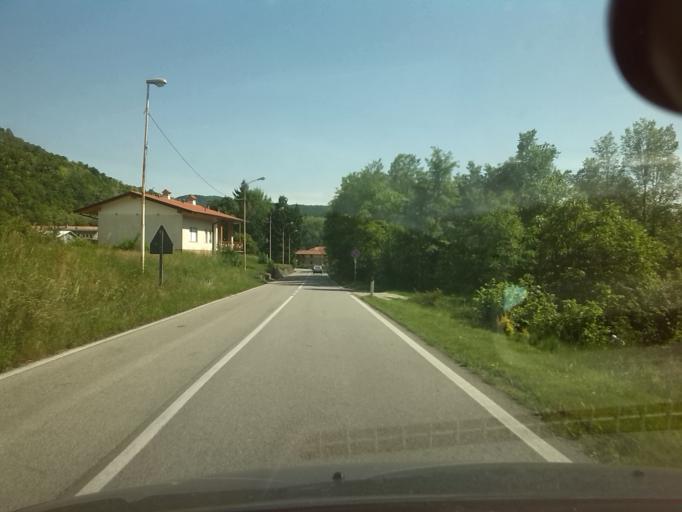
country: IT
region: Friuli Venezia Giulia
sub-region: Provincia di Udine
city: San Pietro al Natisone
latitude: 46.1326
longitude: 13.4850
